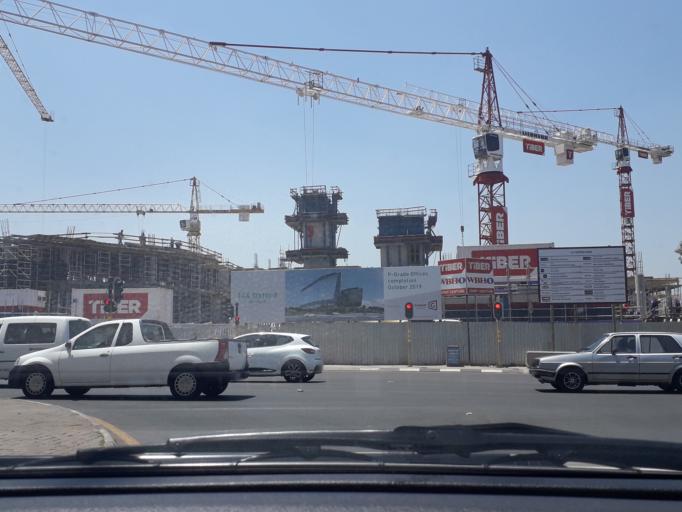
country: ZA
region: Gauteng
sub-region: City of Johannesburg Metropolitan Municipality
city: Johannesburg
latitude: -26.1431
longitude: 28.0434
